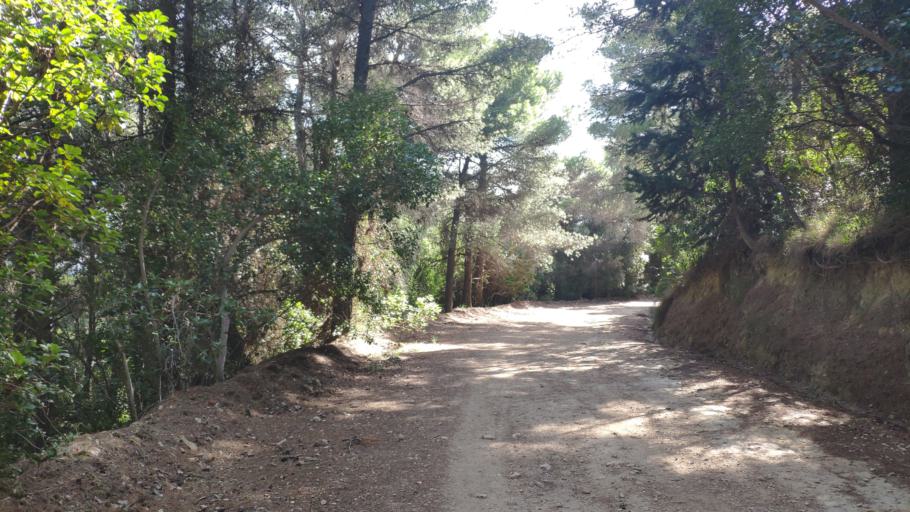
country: GR
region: Attica
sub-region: Nomarchia Anatolikis Attikis
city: Varybobi
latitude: 38.1580
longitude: 23.7764
